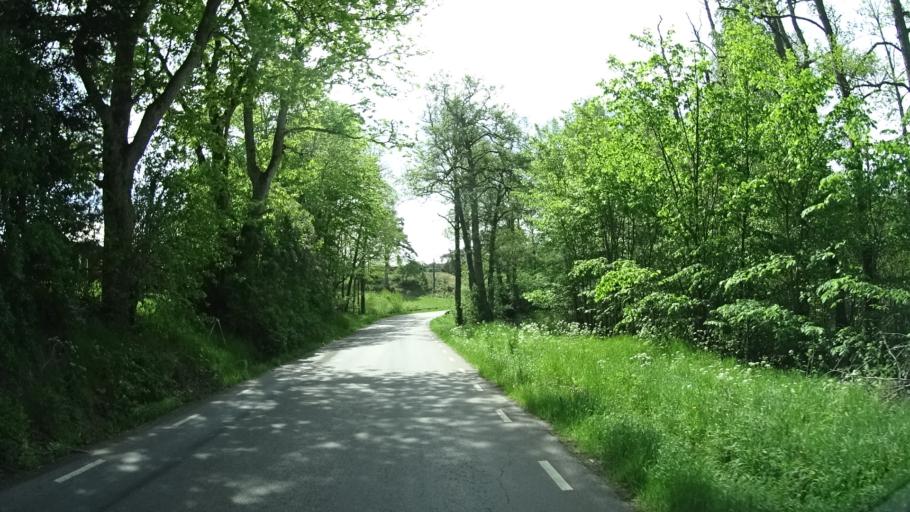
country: SE
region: OEstergoetland
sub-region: Finspangs Kommun
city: Finspang
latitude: 58.7410
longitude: 15.8287
